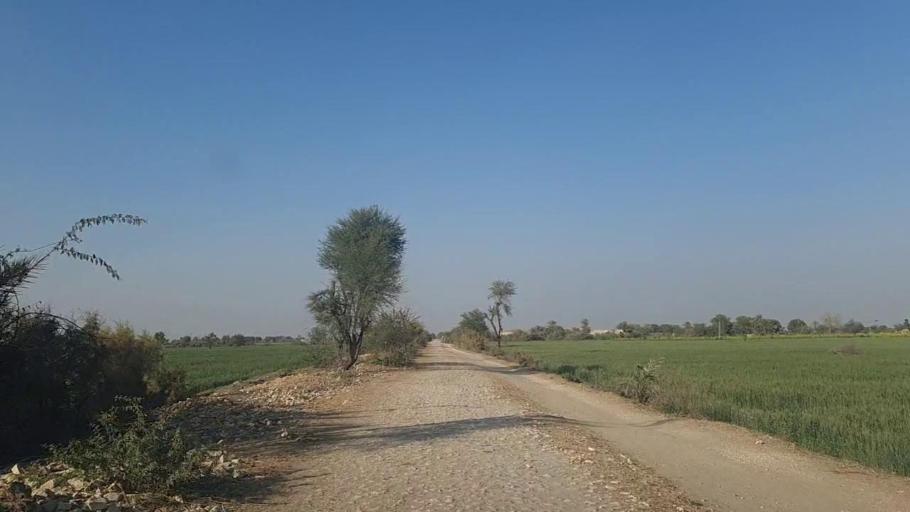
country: PK
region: Sindh
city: Jam Sahib
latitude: 26.3160
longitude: 68.7149
